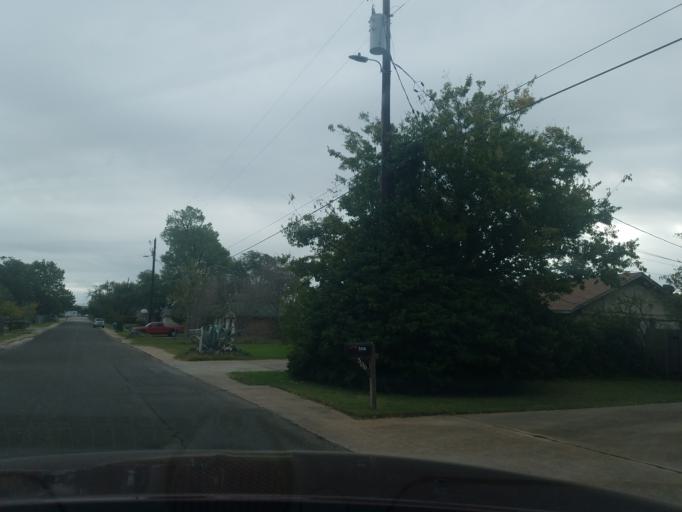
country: US
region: Texas
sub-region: Williamson County
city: Anderson Mill
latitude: 30.4790
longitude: -97.8073
